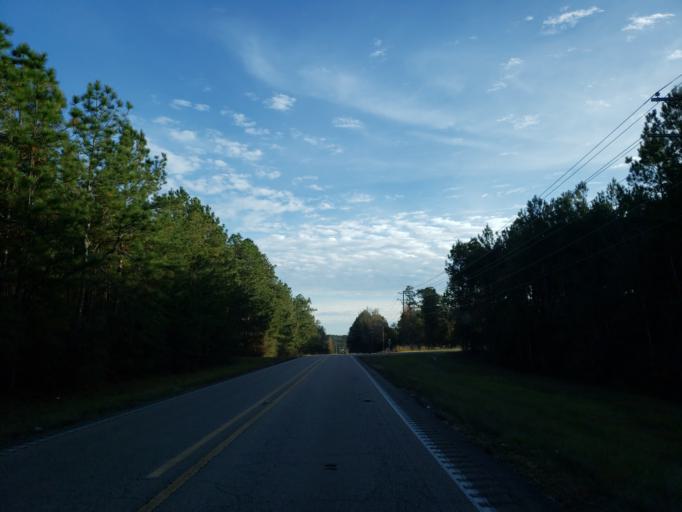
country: US
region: Mississippi
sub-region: Lamar County
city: West Hattiesburg
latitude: 31.3045
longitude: -89.4702
